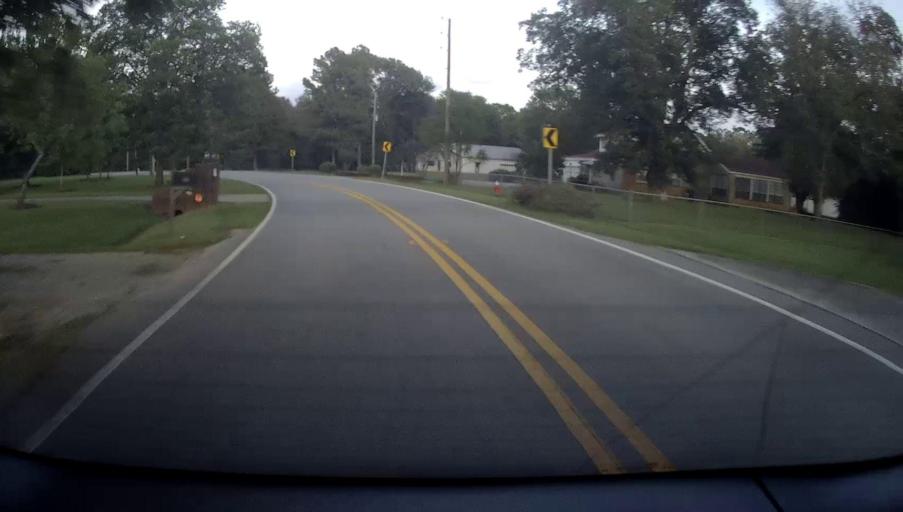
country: US
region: Georgia
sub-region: Houston County
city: Centerville
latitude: 32.6432
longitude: -83.7005
